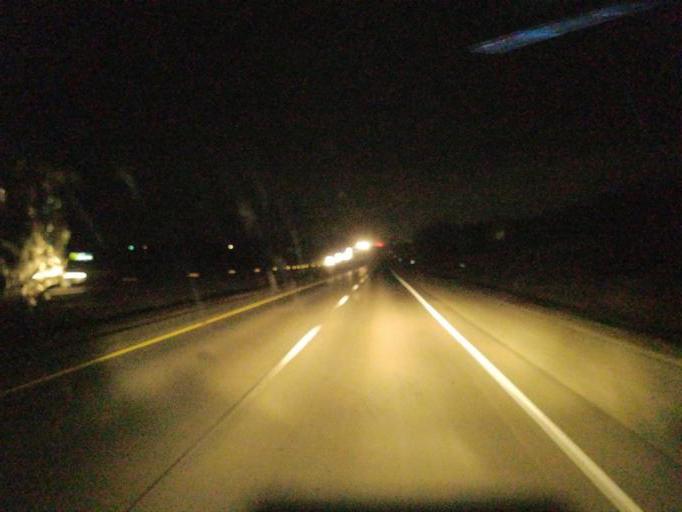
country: US
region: Iowa
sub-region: Dallas County
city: De Soto
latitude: 41.5241
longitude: -94.0607
